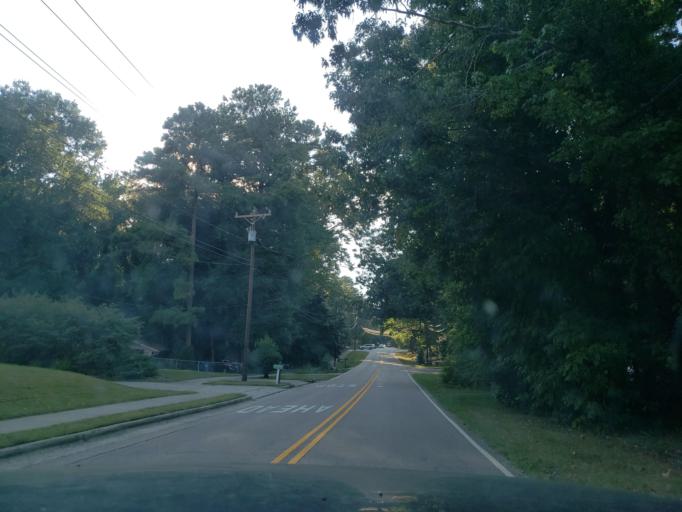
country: US
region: North Carolina
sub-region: Durham County
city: Durham
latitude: 35.9770
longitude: -78.9406
